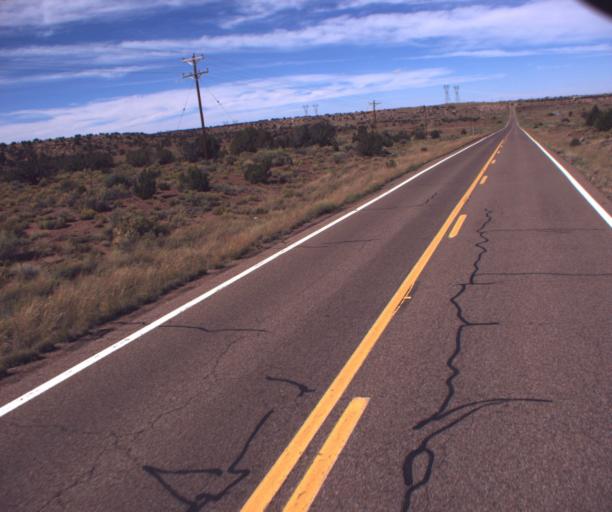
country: US
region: Arizona
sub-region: Apache County
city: Saint Johns
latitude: 34.5403
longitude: -109.6215
